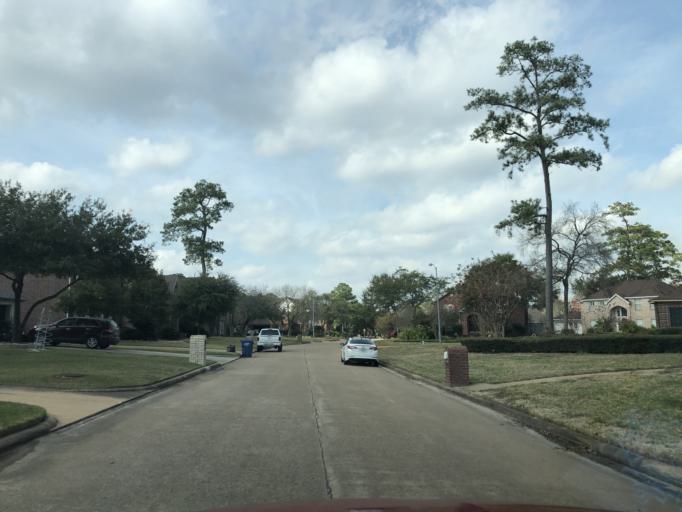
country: US
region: Texas
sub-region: Harris County
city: Tomball
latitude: 30.0313
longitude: -95.5388
